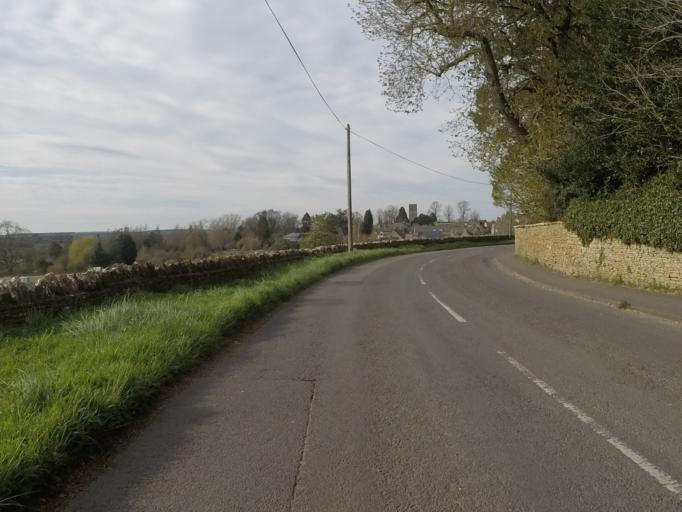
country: GB
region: England
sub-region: Oxfordshire
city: Charlbury
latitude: 51.8685
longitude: -1.4831
